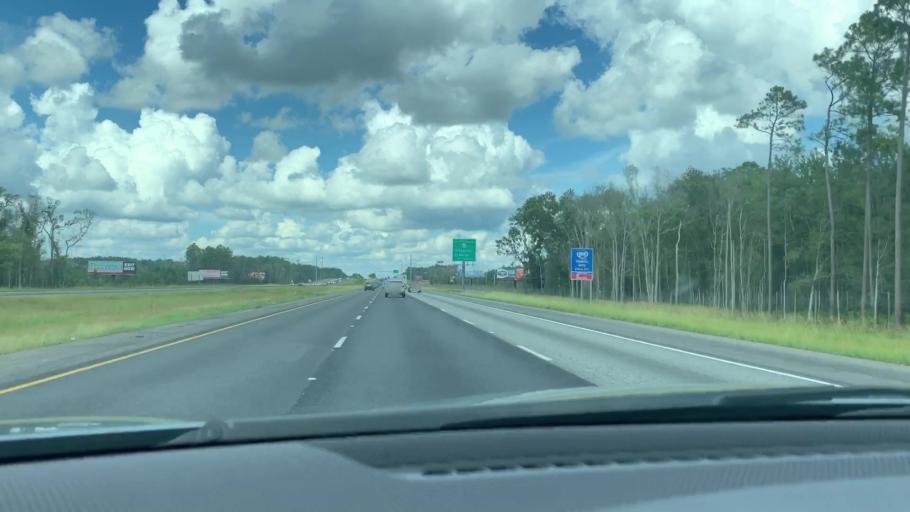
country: US
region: Georgia
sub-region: Camden County
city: Kingsland
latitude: 30.7817
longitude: -81.6565
